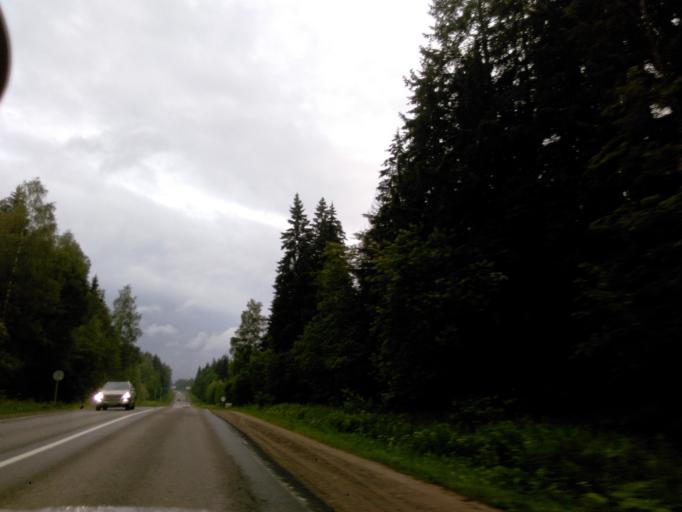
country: RU
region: Moskovskaya
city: Povarovo
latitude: 56.0343
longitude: 36.9688
